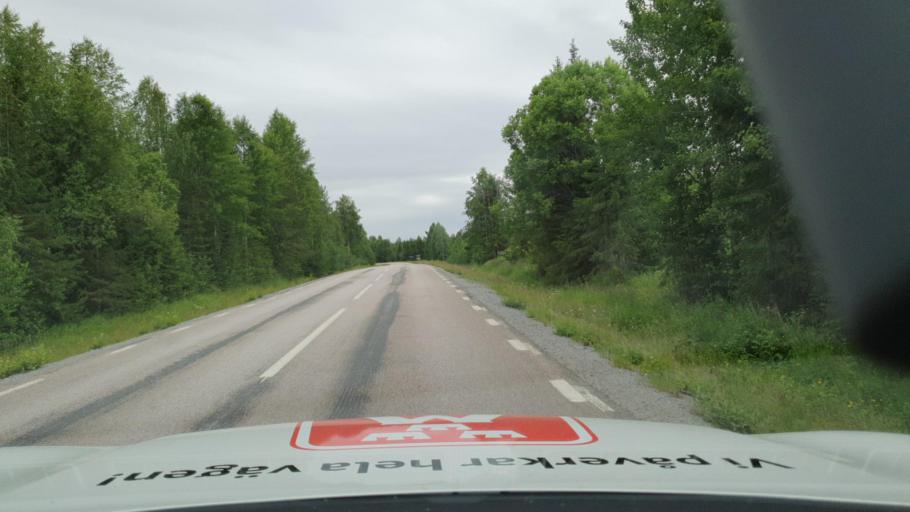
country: SE
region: Vaesterbotten
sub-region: Bjurholms Kommun
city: Bjurholm
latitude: 63.7831
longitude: 19.3073
